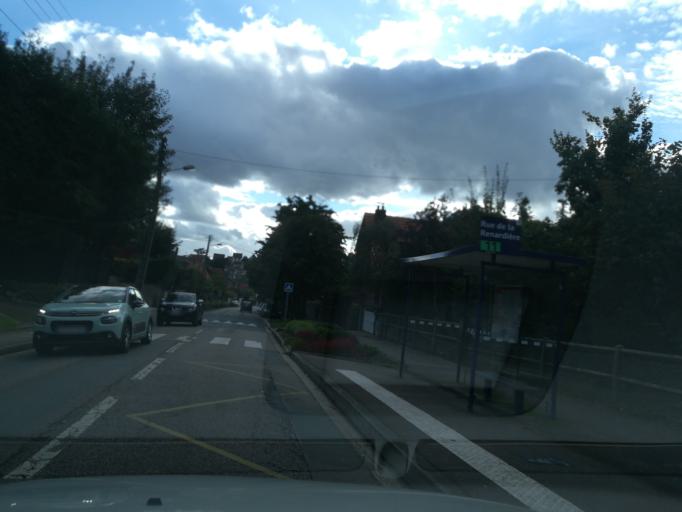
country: FR
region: Haute-Normandie
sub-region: Departement de la Seine-Maritime
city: Mont-Saint-Aignan
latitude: 49.4623
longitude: 1.0961
